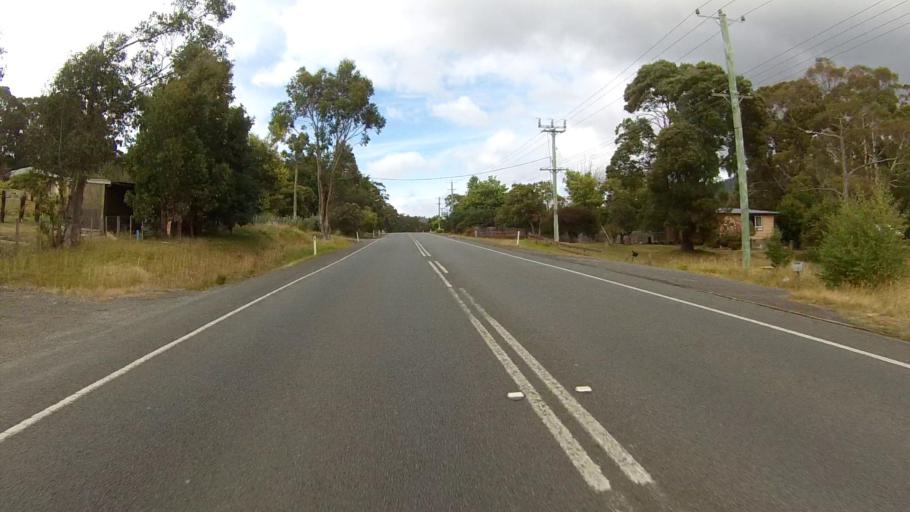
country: AU
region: Tasmania
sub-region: Kingborough
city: Margate
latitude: -43.0768
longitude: 147.2565
